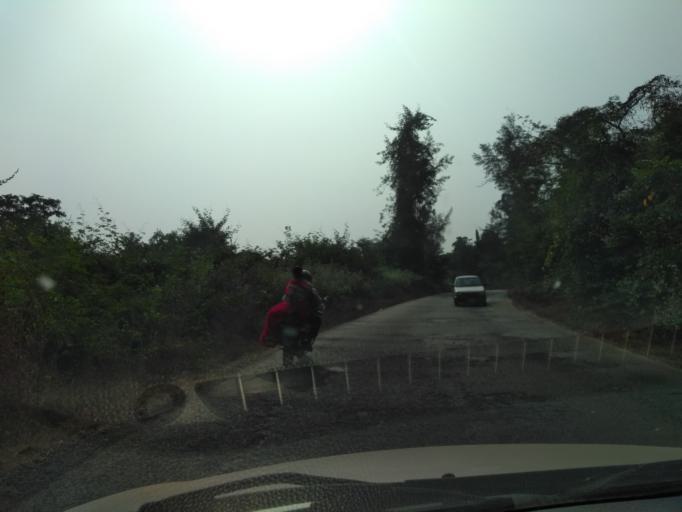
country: IN
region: Maharashtra
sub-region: Sindhudurg
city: Savantvadi
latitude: 15.8150
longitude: 73.9034
